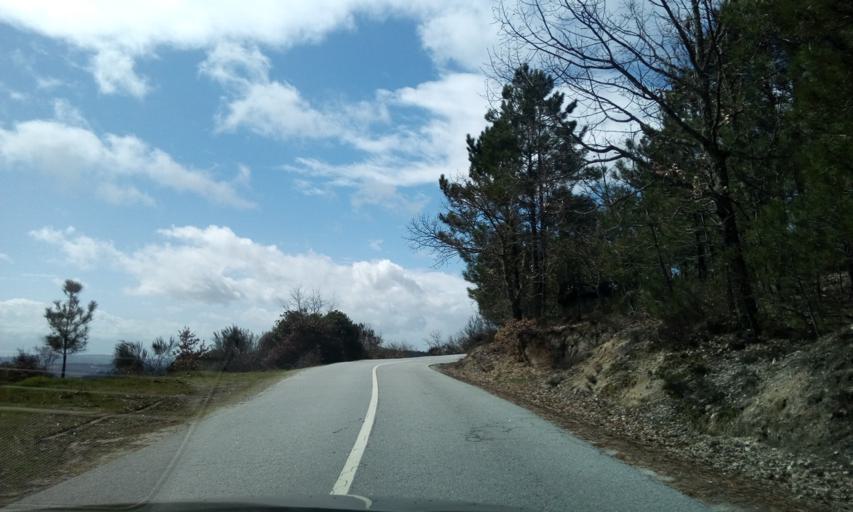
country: PT
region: Guarda
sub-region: Fornos de Algodres
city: Fornos de Algodres
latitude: 40.6334
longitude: -7.5464
